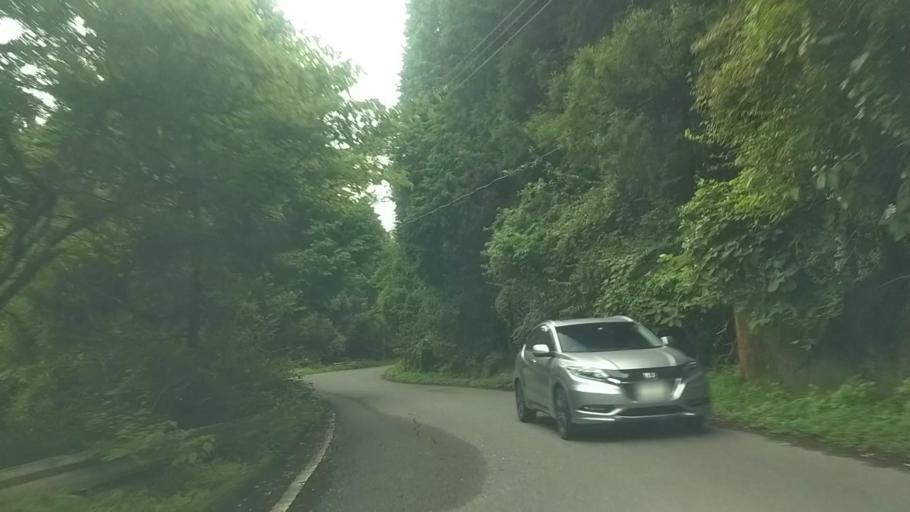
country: JP
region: Chiba
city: Kawaguchi
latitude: 35.2258
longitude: 140.0256
